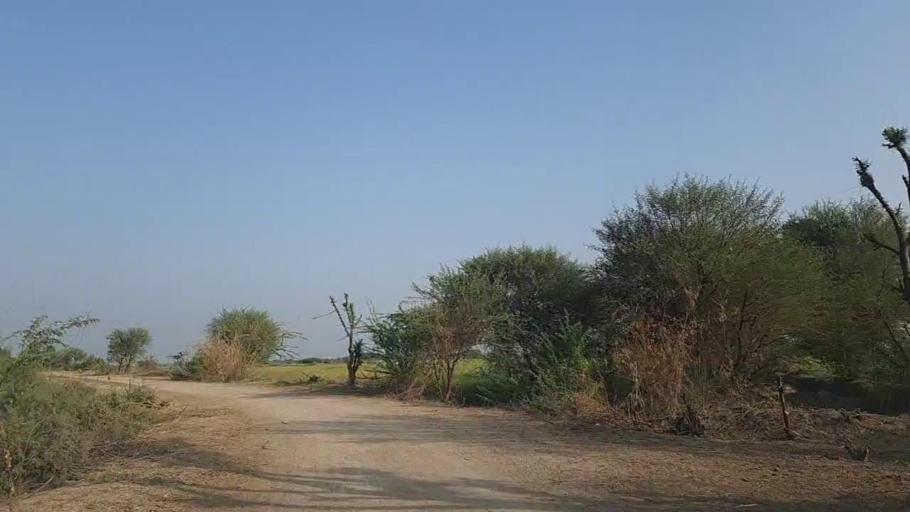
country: PK
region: Sindh
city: Dhoro Naro
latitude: 25.4921
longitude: 69.4969
